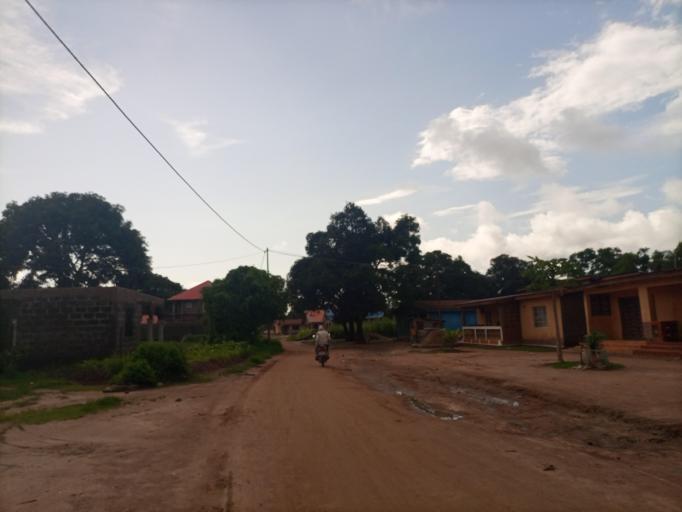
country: SL
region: Northern Province
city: Masoyila
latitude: 8.6060
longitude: -13.1763
